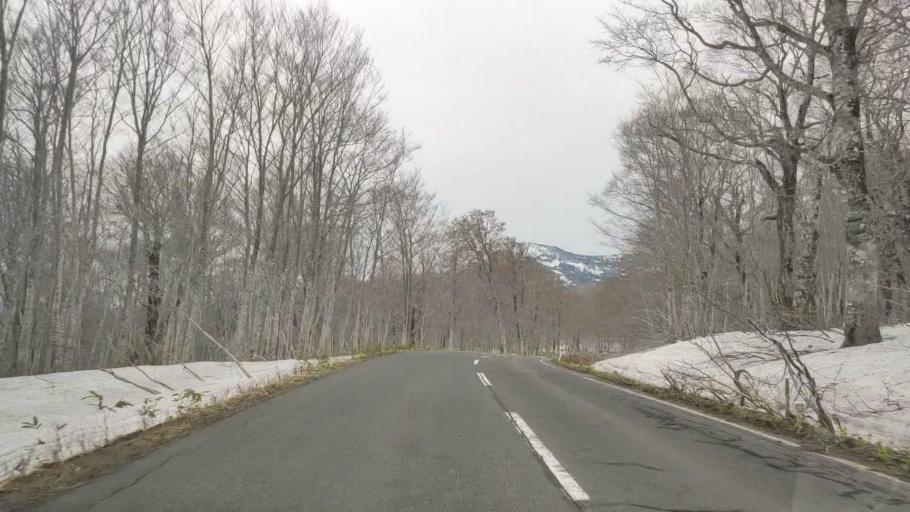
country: JP
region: Aomori
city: Aomori Shi
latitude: 40.6394
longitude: 140.9321
